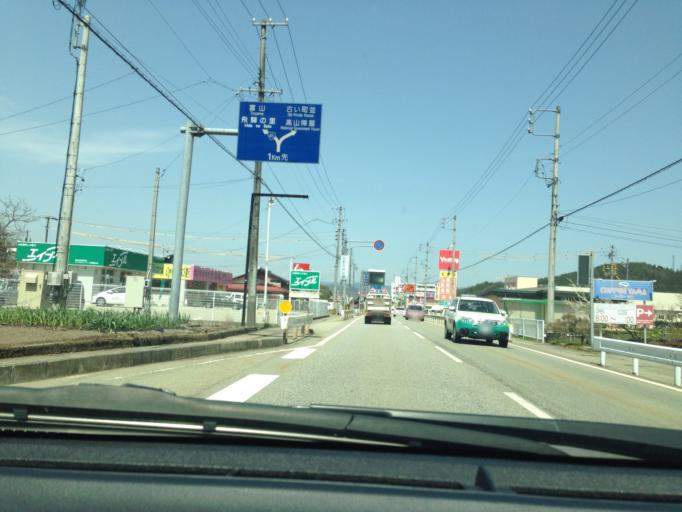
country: JP
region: Gifu
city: Takayama
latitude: 36.1111
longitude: 137.2655
